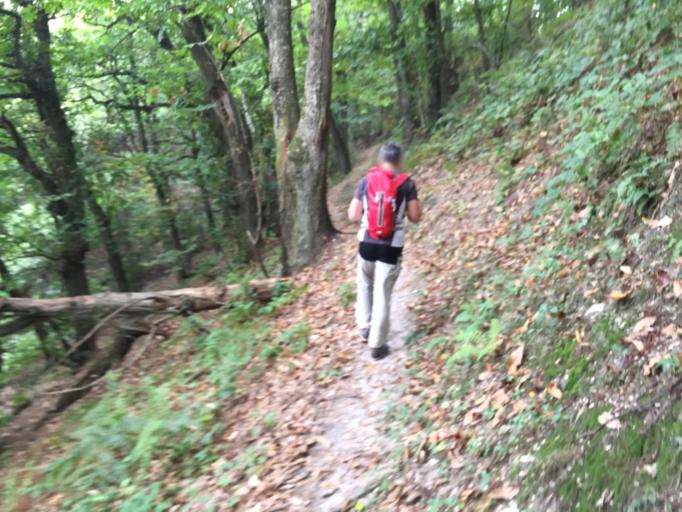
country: IT
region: Piedmont
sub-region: Provincia di Cuneo
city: Chiusa di Pesio
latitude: 44.3260
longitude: 7.6829
